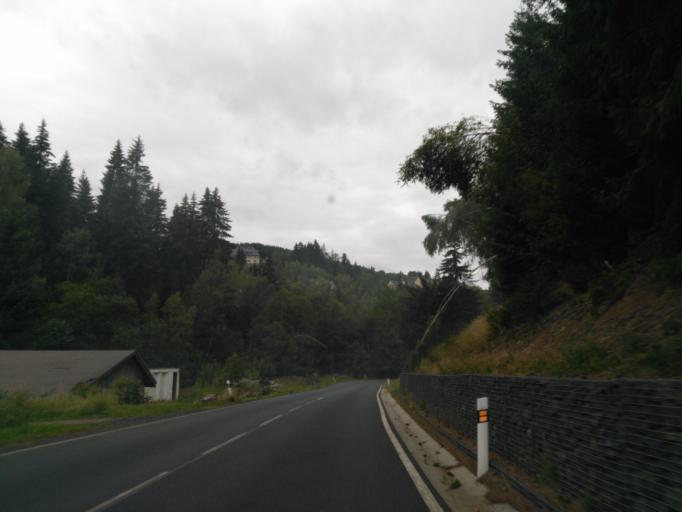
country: DE
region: Saxony
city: Johanngeorgenstadt
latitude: 50.4201
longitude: 12.7313
